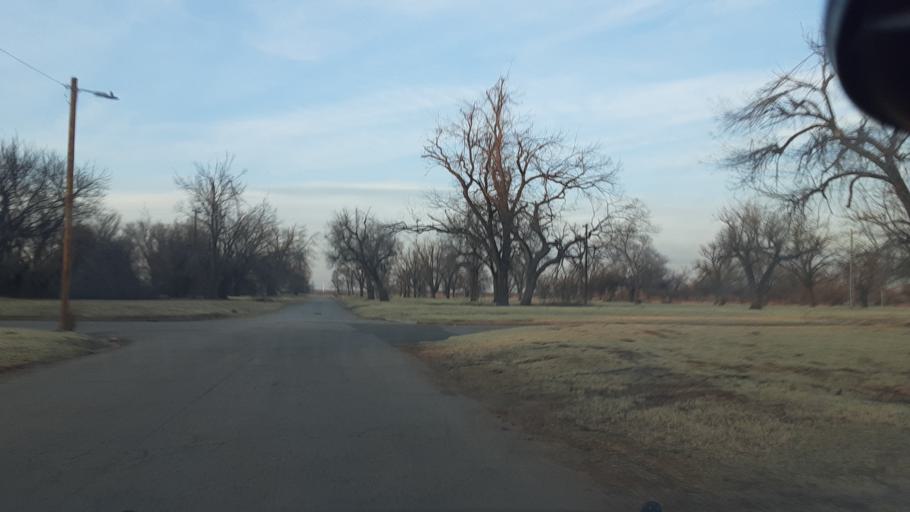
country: US
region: Oklahoma
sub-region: Logan County
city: Guthrie
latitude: 35.8809
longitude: -97.4354
